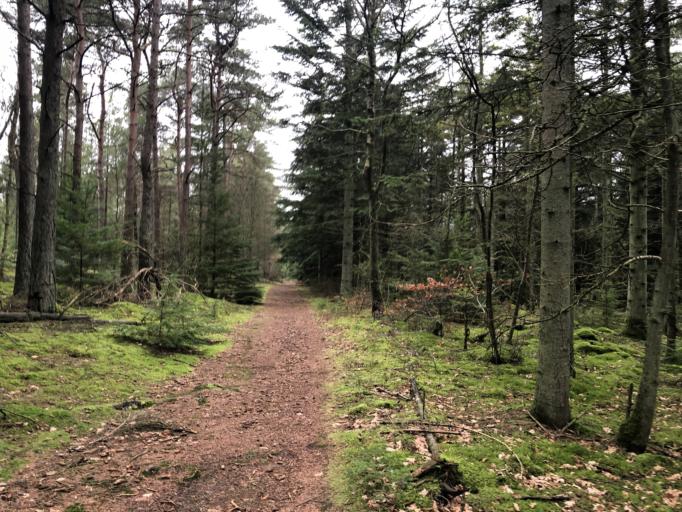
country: DK
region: Central Jutland
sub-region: Holstebro Kommune
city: Ulfborg
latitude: 56.2894
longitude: 8.1756
